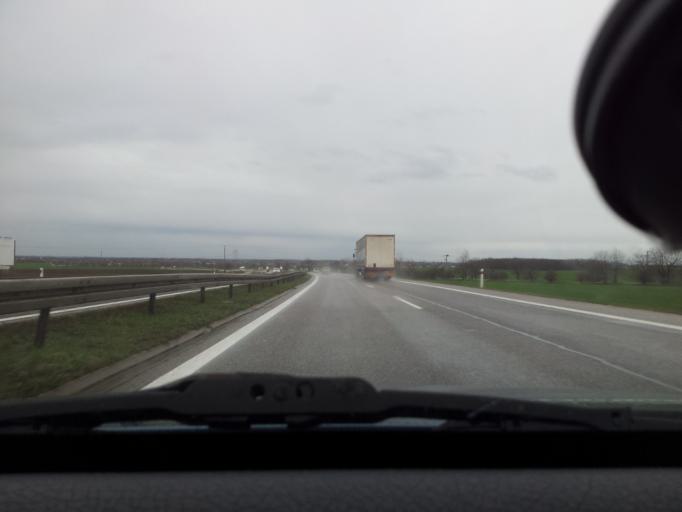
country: SK
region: Nitriansky
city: Sellye
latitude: 48.2850
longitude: 17.8569
